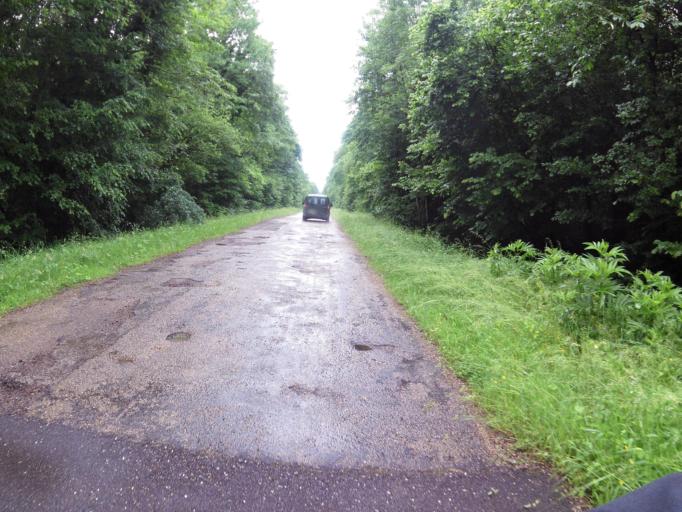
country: FR
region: Champagne-Ardenne
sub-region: Departement de la Marne
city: Sermaize-les-Bains
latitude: 48.7569
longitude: 4.9542
